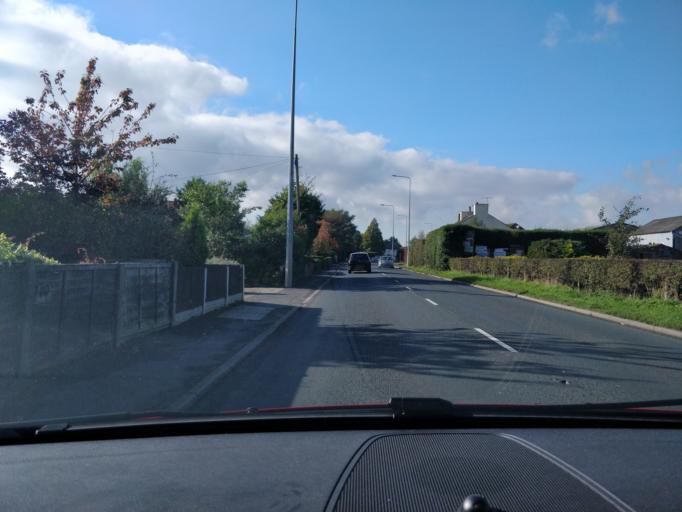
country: GB
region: England
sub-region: Sefton
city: Southport
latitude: 53.6182
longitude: -2.9468
